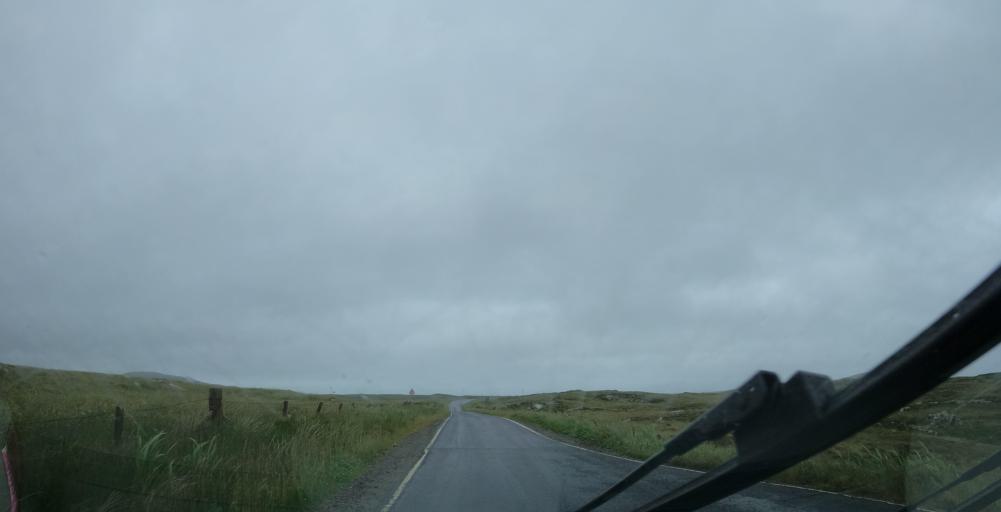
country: GB
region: Scotland
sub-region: Eilean Siar
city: Barra
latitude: 56.9786
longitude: -7.4175
